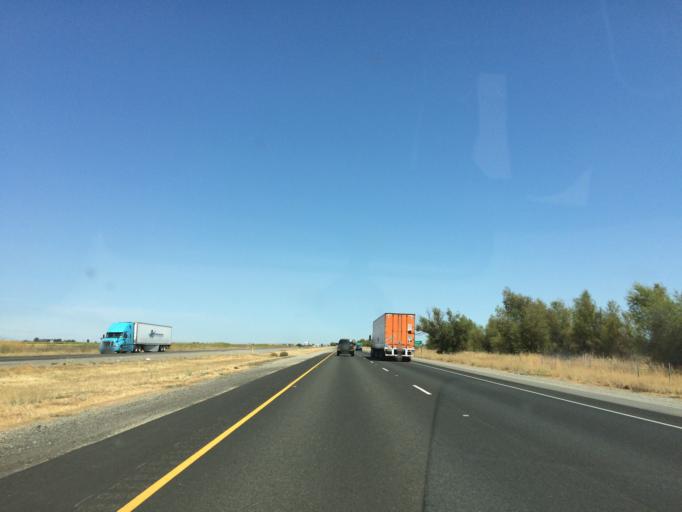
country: US
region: California
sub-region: Colusa County
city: Maxwell
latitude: 39.3840
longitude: -122.1929
